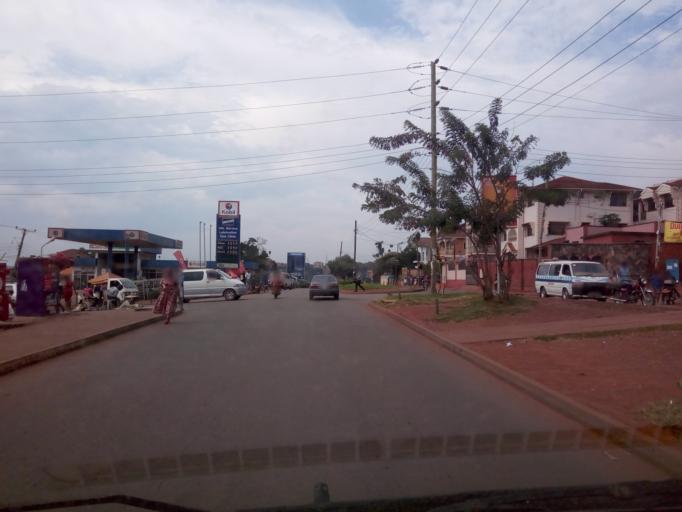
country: UG
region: Central Region
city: Kampala Central Division
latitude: 0.3418
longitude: 32.5891
